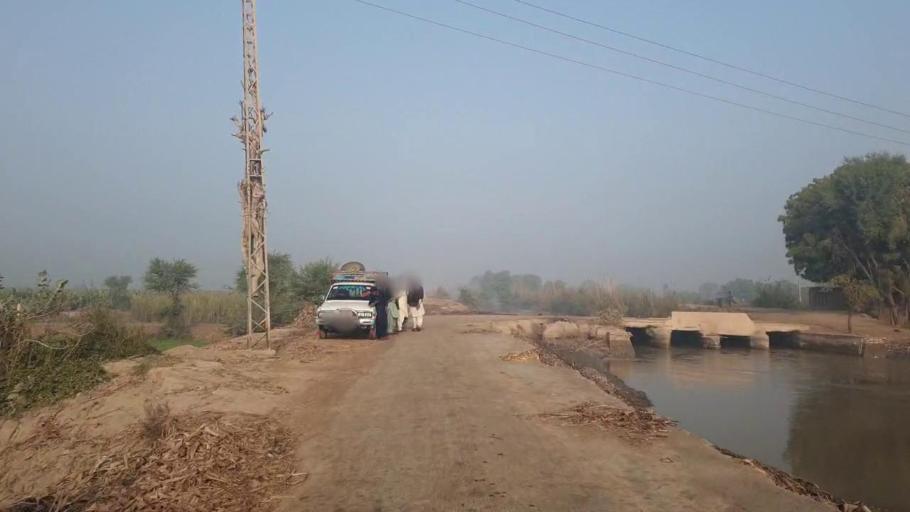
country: PK
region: Sindh
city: Tando Adam
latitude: 25.8103
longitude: 68.6318
